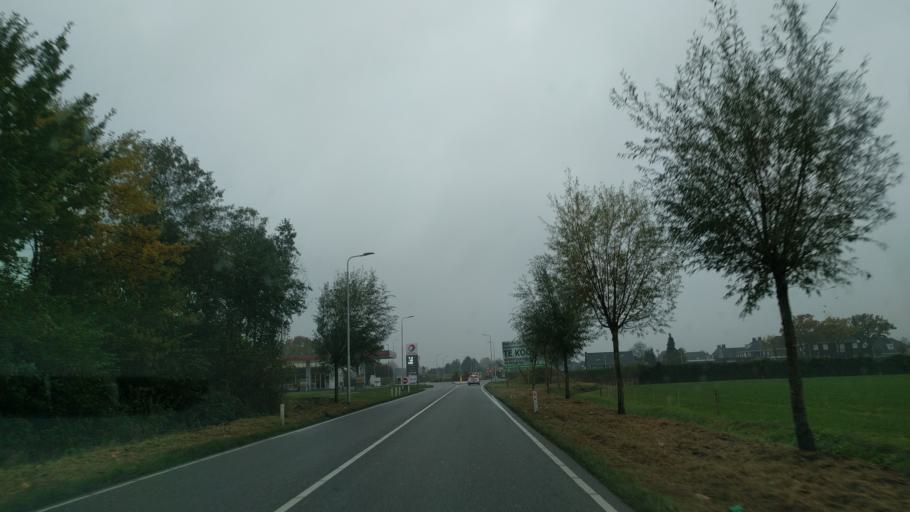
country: NL
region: North Brabant
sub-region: Gemeente Rucphen
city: Rucphen
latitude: 51.5472
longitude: 4.6039
